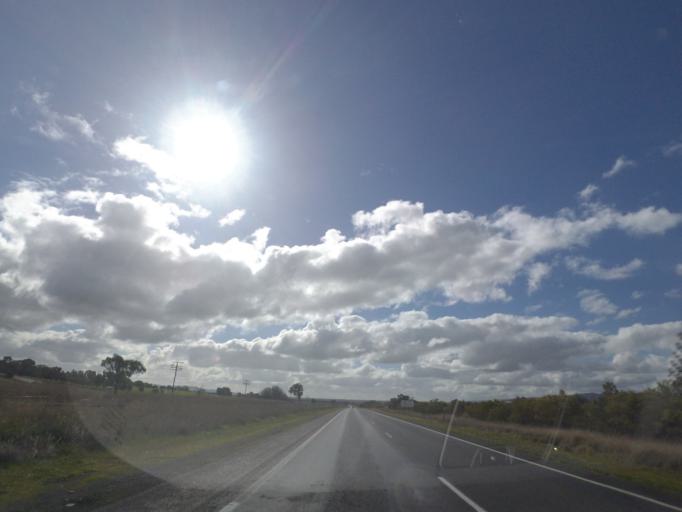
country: AU
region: New South Wales
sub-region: Greater Hume Shire
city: Jindera
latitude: -35.9567
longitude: 147.0043
